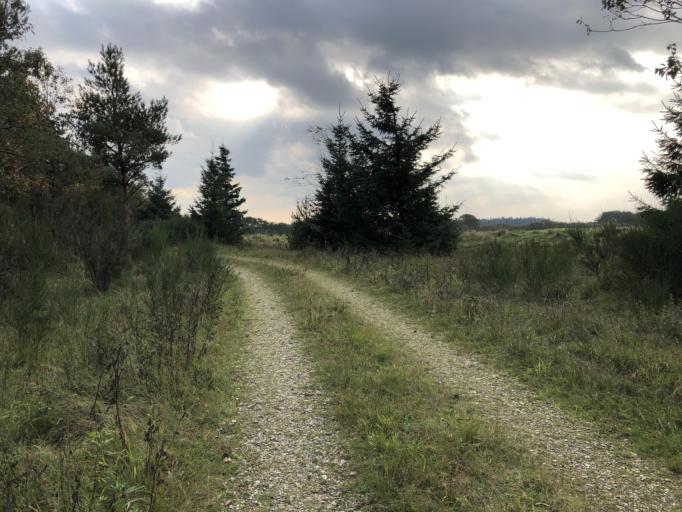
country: DK
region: Central Jutland
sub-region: Holstebro Kommune
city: Ulfborg
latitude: 56.2182
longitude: 8.4356
